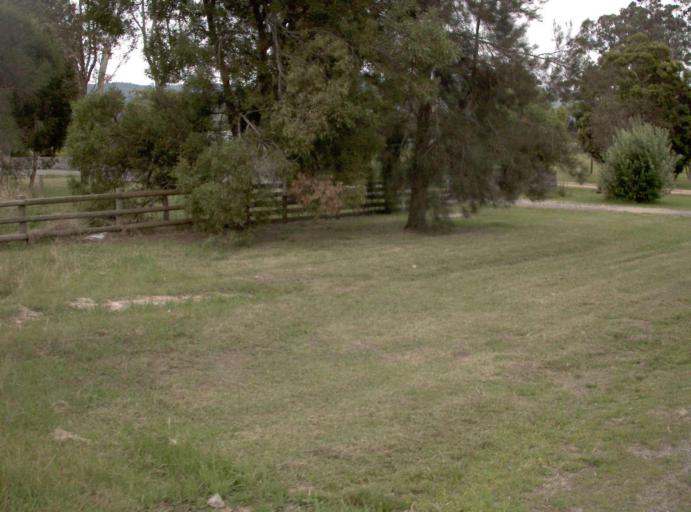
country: AU
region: New South Wales
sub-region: Bombala
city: Bombala
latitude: -37.5149
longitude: 149.1686
